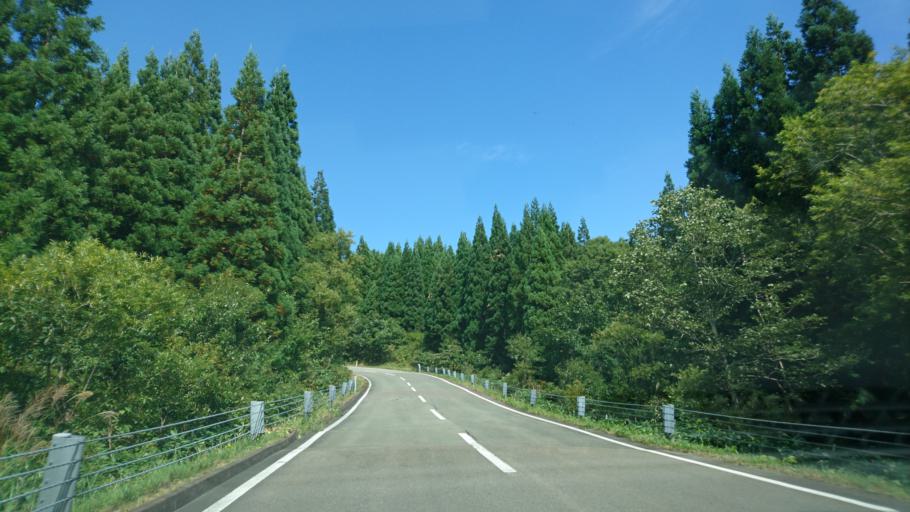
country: JP
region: Akita
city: Yuzawa
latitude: 38.9749
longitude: 140.7101
